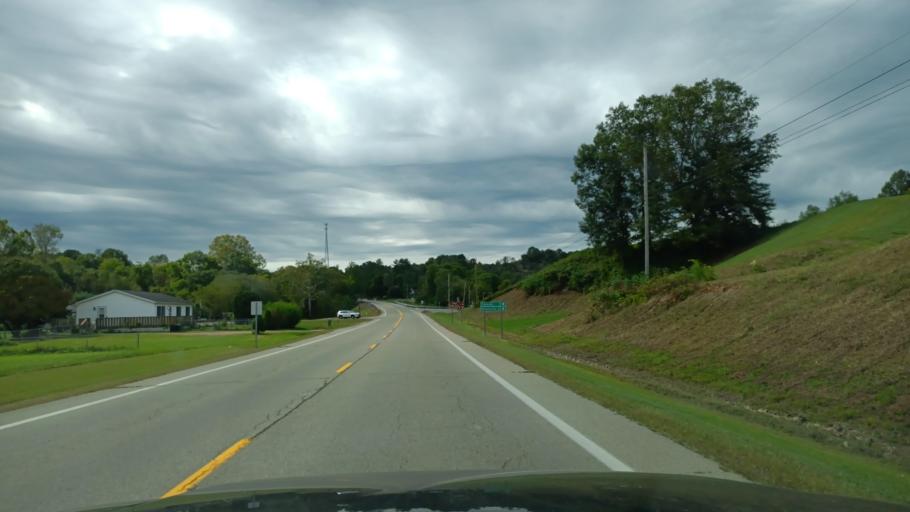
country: US
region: Ohio
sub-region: Vinton County
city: McArthur
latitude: 39.2386
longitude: -82.3837
